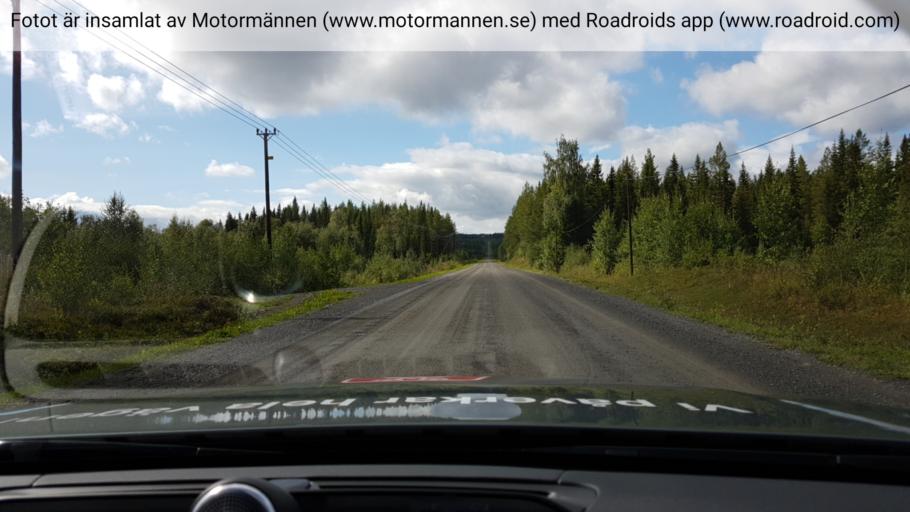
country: SE
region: Jaemtland
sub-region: OEstersunds Kommun
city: Lit
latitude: 63.6229
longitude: 15.1568
